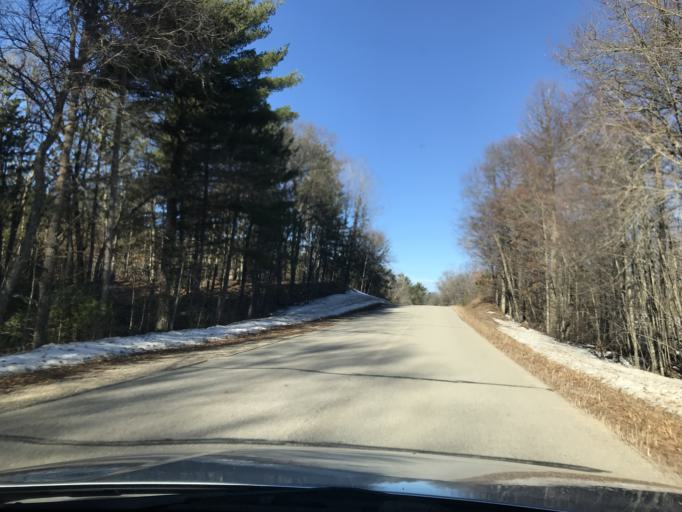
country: US
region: Wisconsin
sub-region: Marinette County
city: Niagara
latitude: 45.3906
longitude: -88.0754
